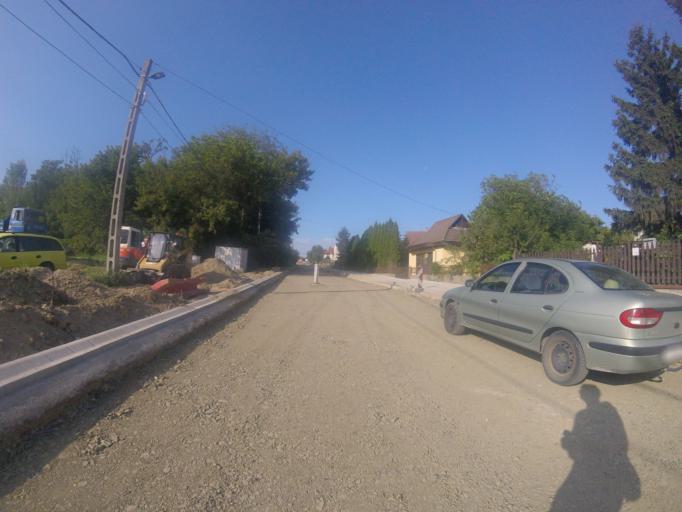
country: HU
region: Pest
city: Veresegyhaz
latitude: 47.6519
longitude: 19.2778
